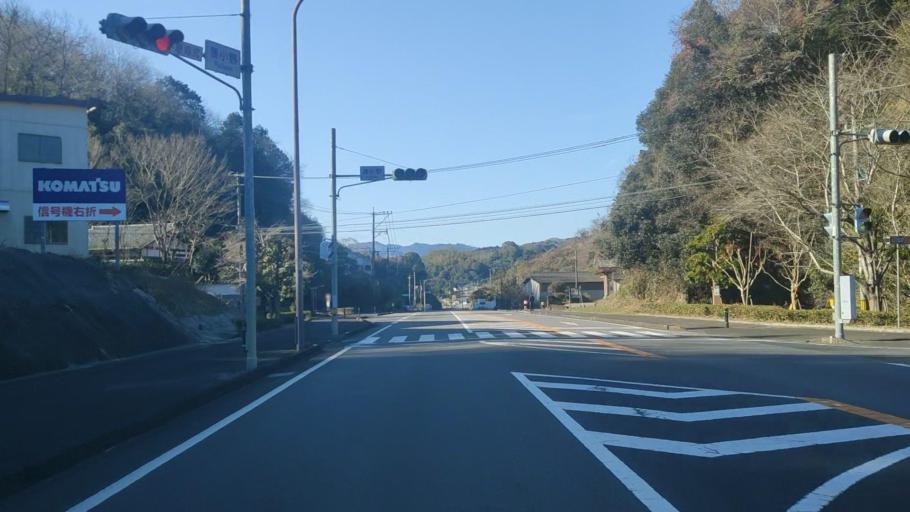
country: JP
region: Oita
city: Usuki
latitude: 33.0621
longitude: 131.6664
